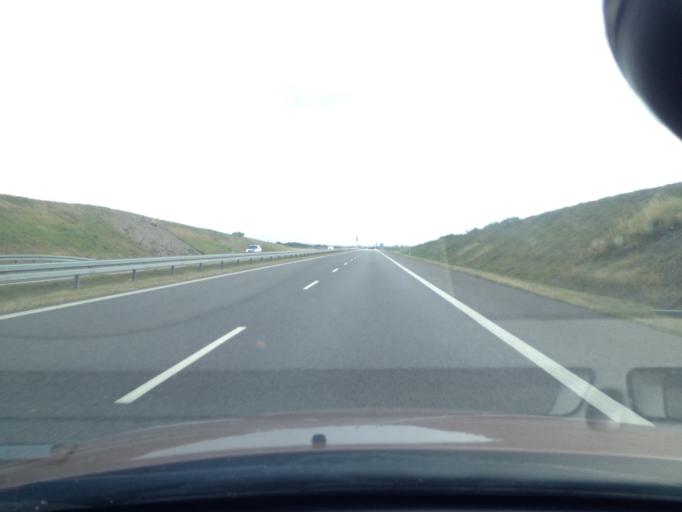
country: PL
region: West Pomeranian Voivodeship
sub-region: Powiat pyrzycki
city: Kozielice
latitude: 53.0662
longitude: 14.8620
